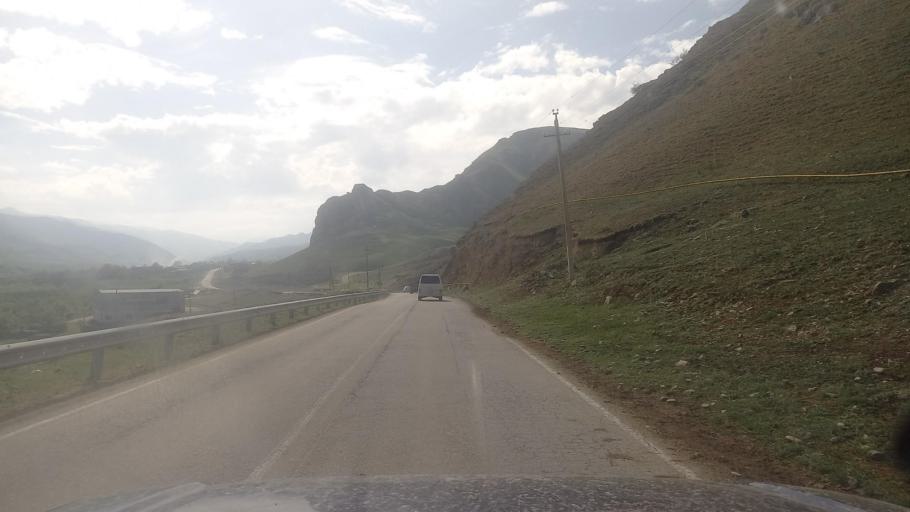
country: RU
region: Kabardino-Balkariya
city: Kamennomostskoye
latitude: 43.7340
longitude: 42.9683
